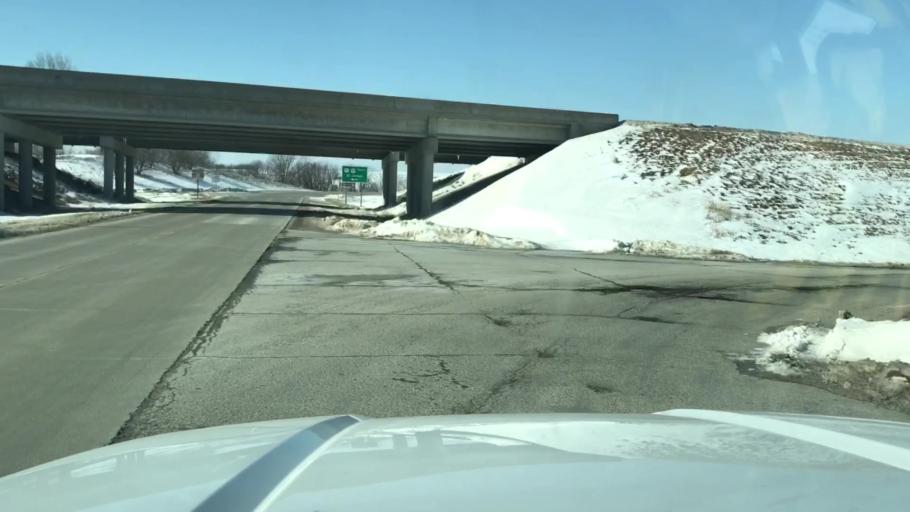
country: US
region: Missouri
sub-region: Andrew County
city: Savannah
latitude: 39.9618
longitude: -94.8606
